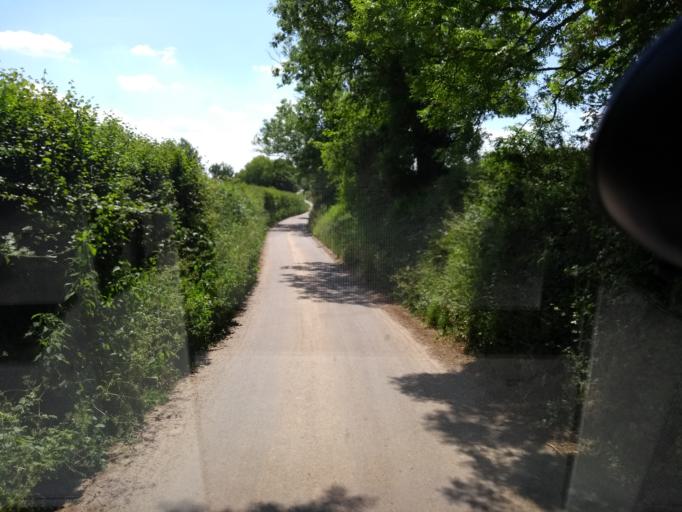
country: GB
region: England
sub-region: Somerset
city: North Petherton
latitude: 51.0580
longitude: -2.9999
